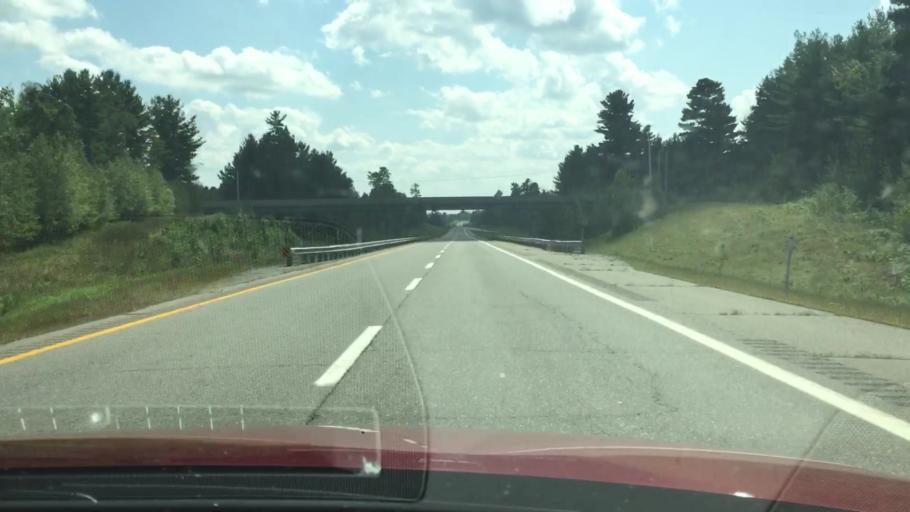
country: US
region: Maine
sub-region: Penobscot County
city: Lincoln
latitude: 45.3767
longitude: -68.6055
